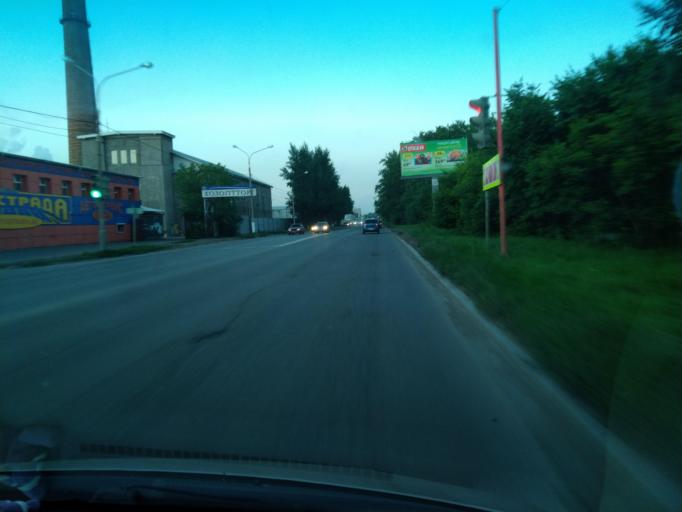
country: RU
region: Krasnoyarskiy
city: Krasnoyarsk
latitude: 55.9899
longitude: 92.9126
